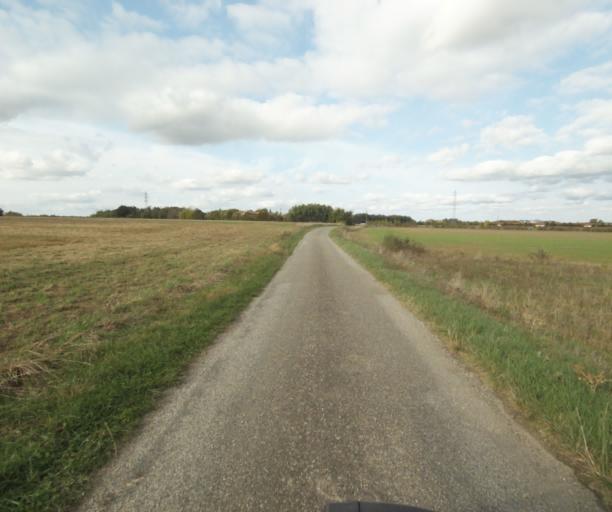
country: FR
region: Midi-Pyrenees
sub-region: Departement du Tarn-et-Garonne
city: Verdun-sur-Garonne
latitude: 43.8395
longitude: 1.1606
